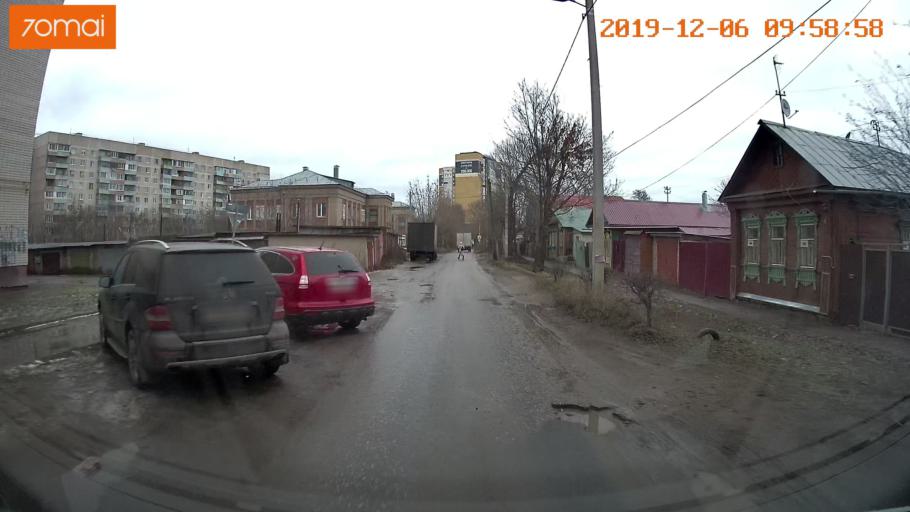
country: RU
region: Ivanovo
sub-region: Gorod Ivanovo
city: Ivanovo
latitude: 56.9839
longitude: 40.9763
